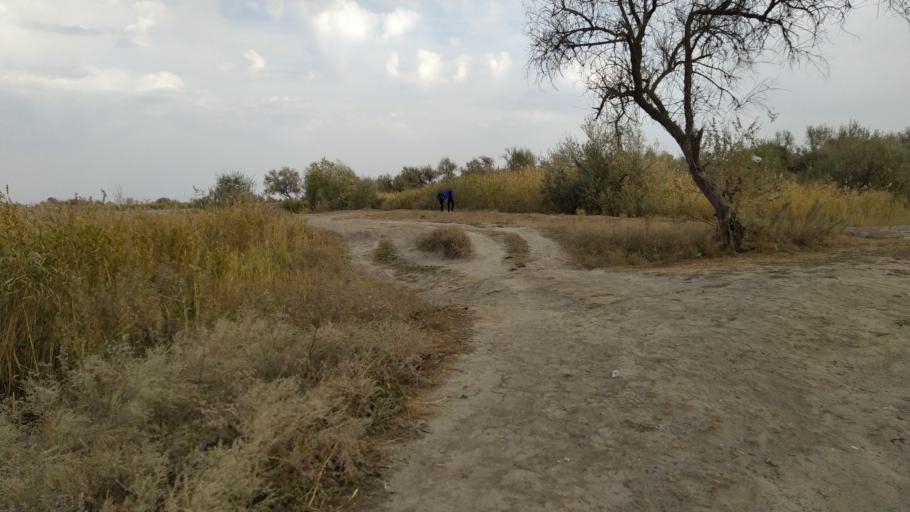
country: RU
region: Rostov
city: Kuleshovka
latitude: 47.1415
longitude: 39.5787
